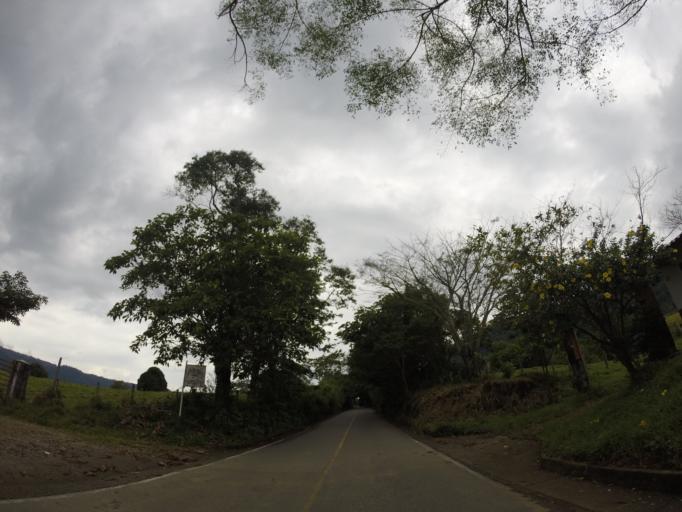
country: CO
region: Caldas
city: Victoria
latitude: 5.3196
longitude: -74.9222
